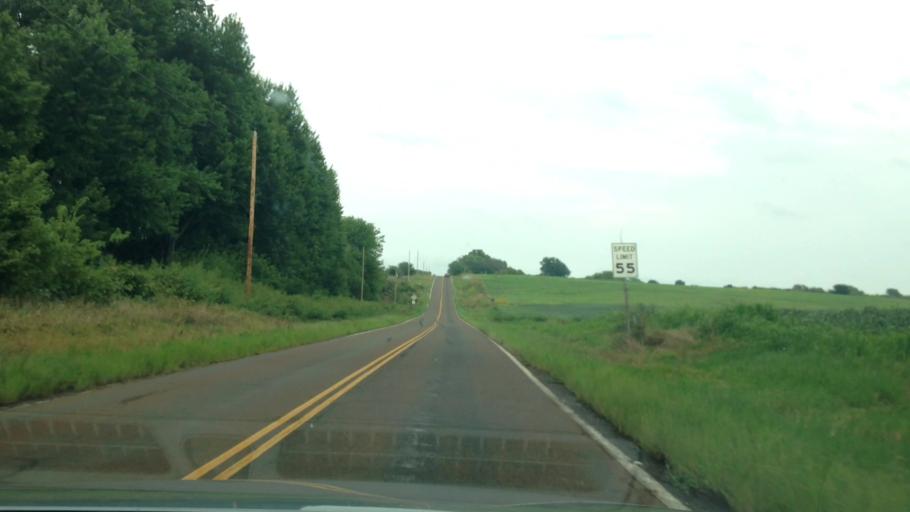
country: US
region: Missouri
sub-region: Clay County
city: Smithville
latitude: 39.4050
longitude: -94.6554
